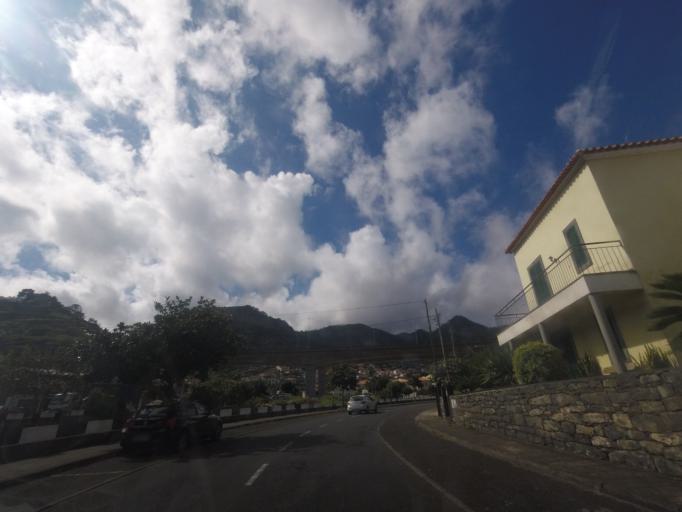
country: PT
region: Madeira
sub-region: Machico
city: Machico
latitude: 32.7310
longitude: -16.7763
